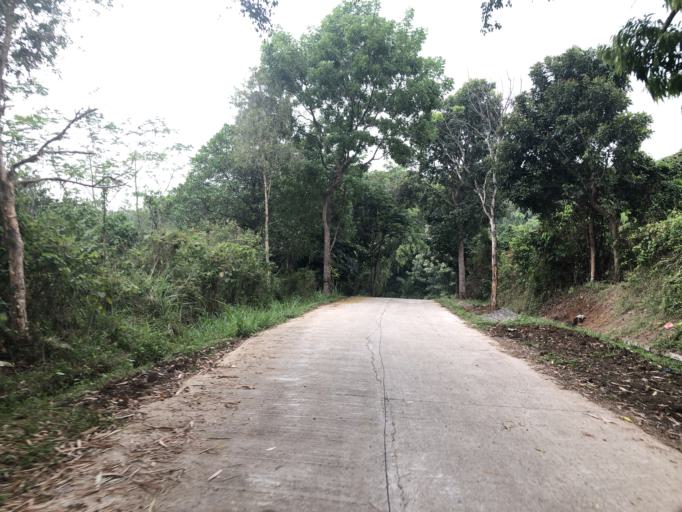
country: ID
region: West Java
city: Ciampea
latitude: -6.5500
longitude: 106.7147
